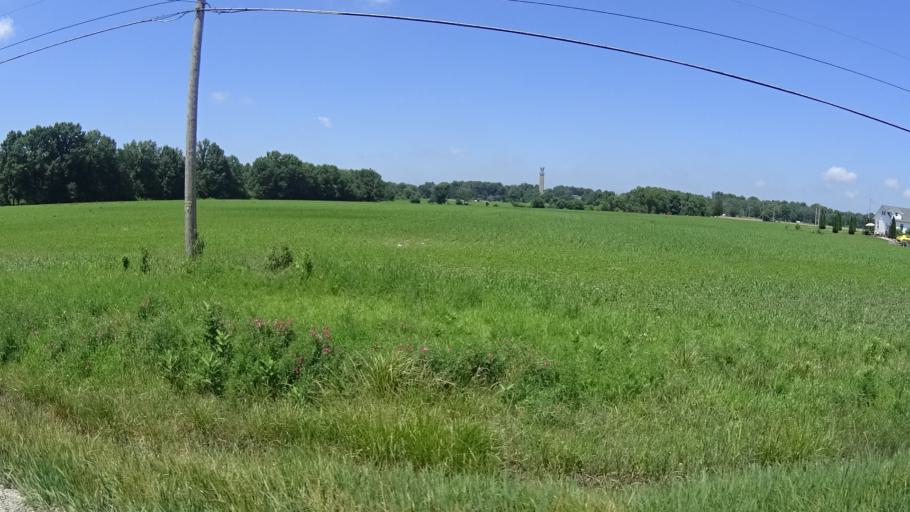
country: US
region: Ohio
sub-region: Huron County
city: Wakeman
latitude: 41.3285
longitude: -82.3749
